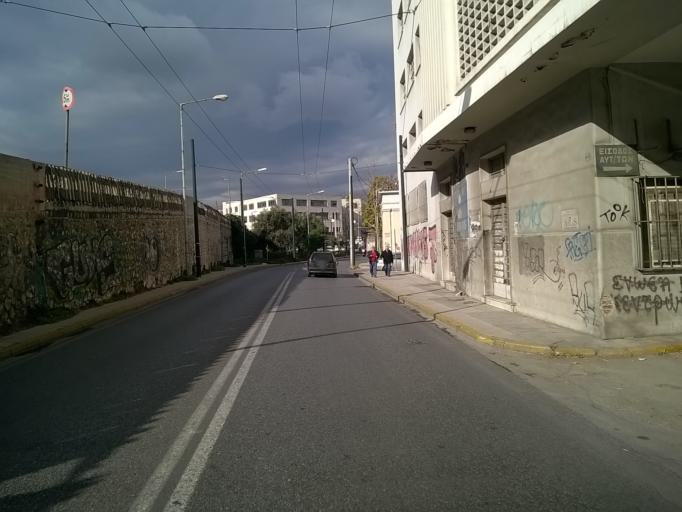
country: GR
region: Attica
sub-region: Nomos Attikis
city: Piraeus
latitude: 37.9488
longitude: 23.6526
